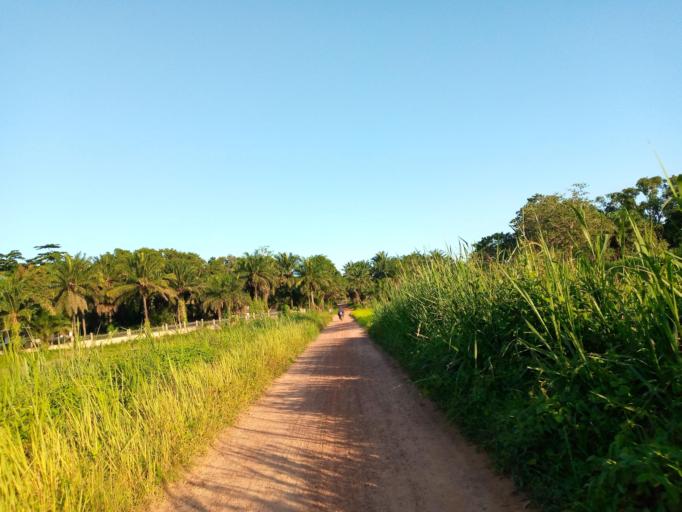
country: SL
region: Northern Province
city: Yonibana
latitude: 8.4482
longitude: -12.2422
